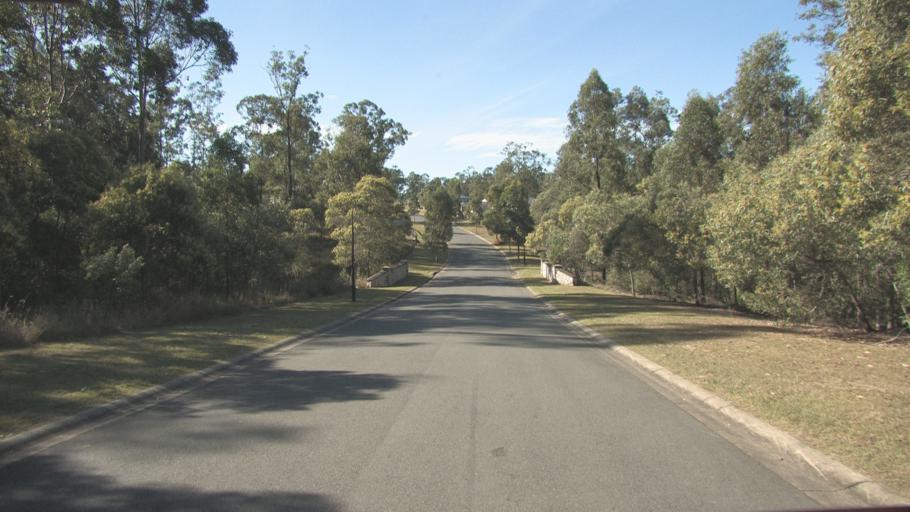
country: AU
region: Queensland
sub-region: Ipswich
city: Springfield Lakes
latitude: -27.7254
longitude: 152.9235
